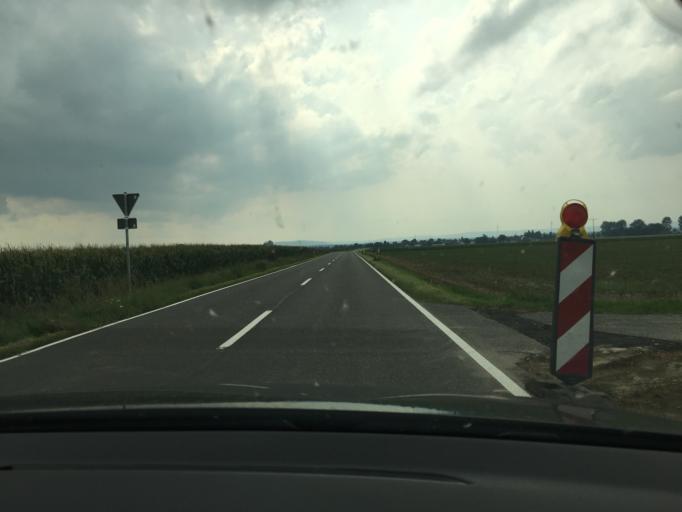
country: DE
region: North Rhine-Westphalia
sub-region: Regierungsbezirk Koln
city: Merzenich
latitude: 50.7896
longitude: 6.5670
